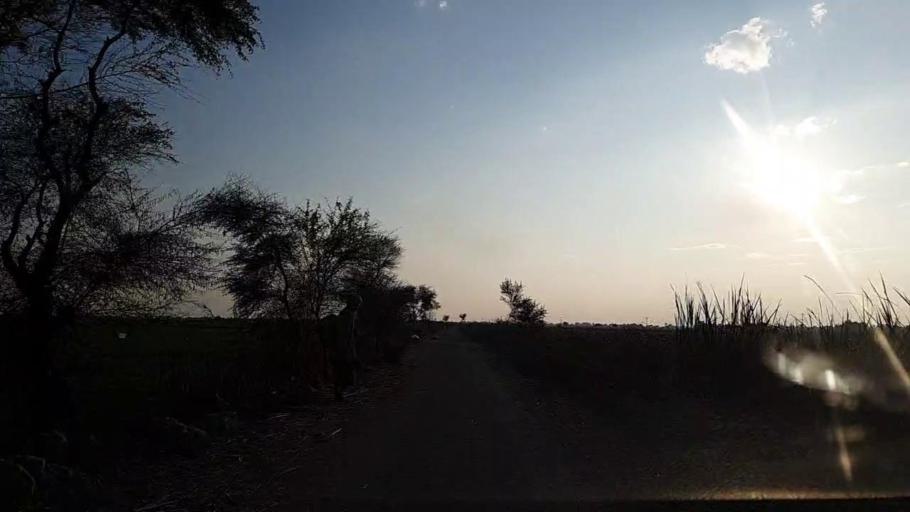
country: PK
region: Sindh
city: Sanghar
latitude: 26.2628
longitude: 68.9795
